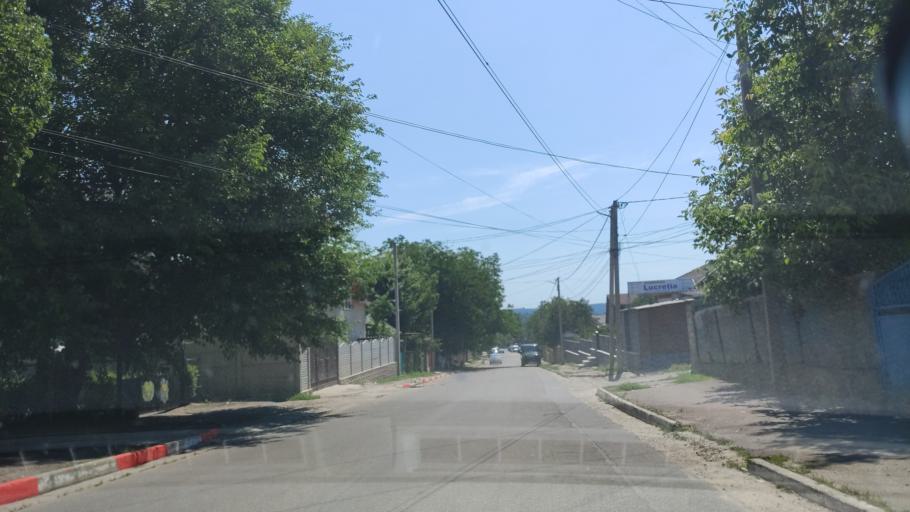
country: MD
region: Raionul Soroca
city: Soroca
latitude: 48.1685
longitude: 28.3006
